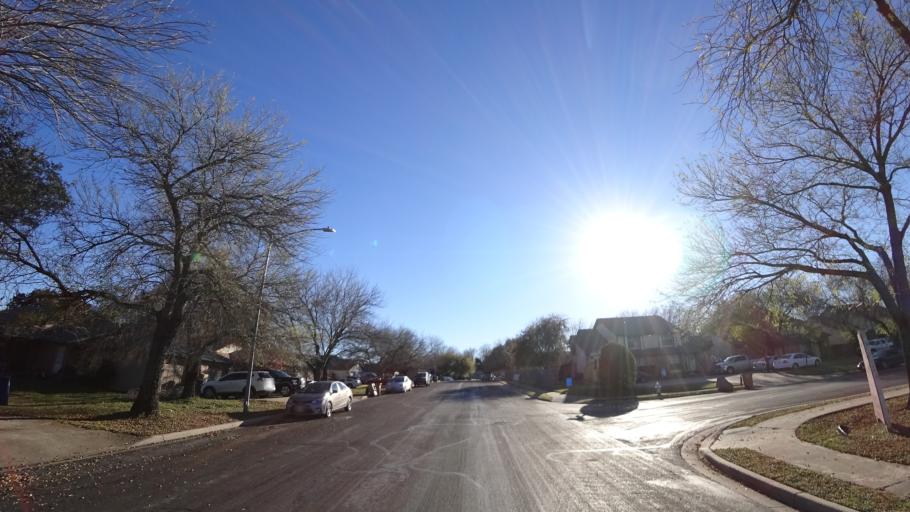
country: US
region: Texas
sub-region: Travis County
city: Wells Branch
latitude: 30.3994
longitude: -97.7018
